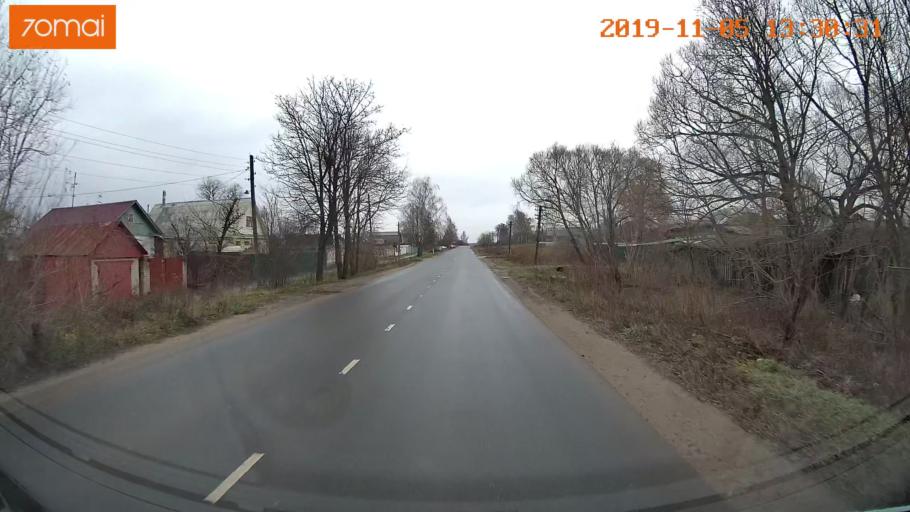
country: RU
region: Ivanovo
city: Shuya
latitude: 56.8675
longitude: 41.3957
